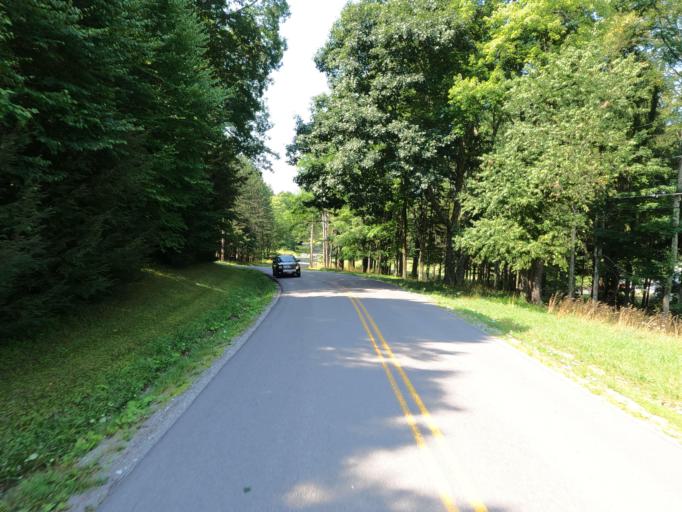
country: US
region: Maryland
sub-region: Garrett County
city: Oakland
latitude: 39.5026
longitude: -79.4099
